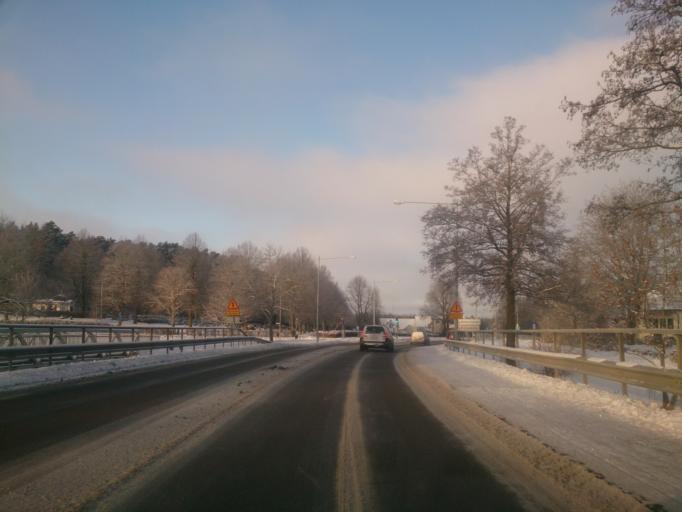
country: SE
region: OEstergoetland
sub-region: Soderkopings Kommun
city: Soederkoeping
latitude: 58.4801
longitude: 16.3148
